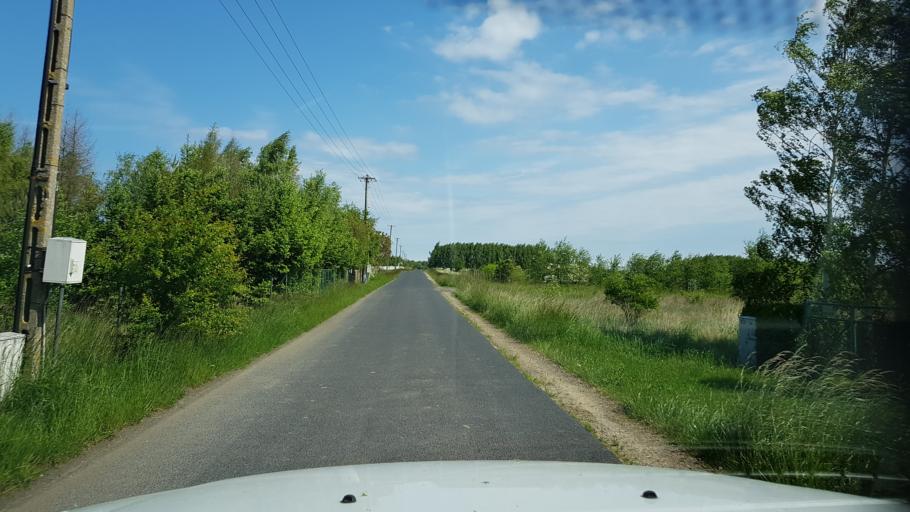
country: PL
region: West Pomeranian Voivodeship
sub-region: Powiat kolobrzeski
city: Ustronie Morskie
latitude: 54.2232
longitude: 15.8950
